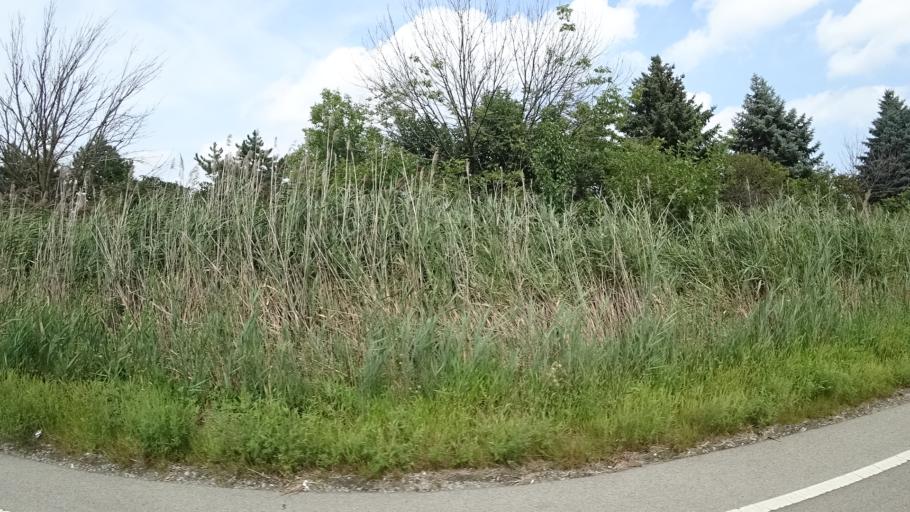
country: US
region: Illinois
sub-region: Cook County
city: Orland Park
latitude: 41.6299
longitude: -87.8837
